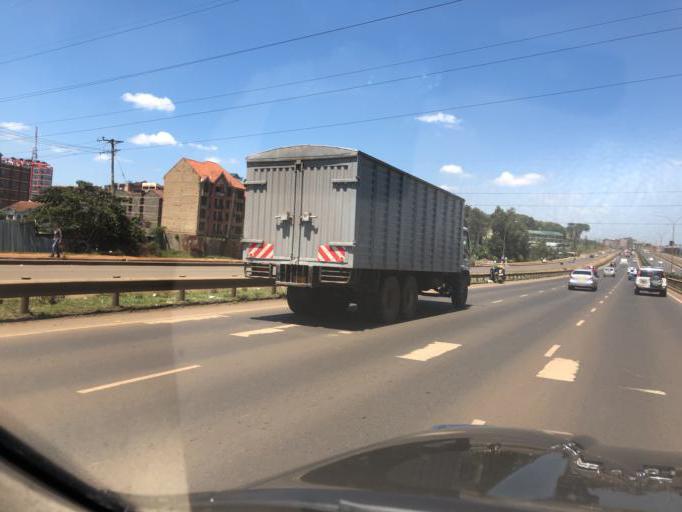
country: KE
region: Kiambu
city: Kiambu
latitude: -1.2113
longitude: 36.9065
